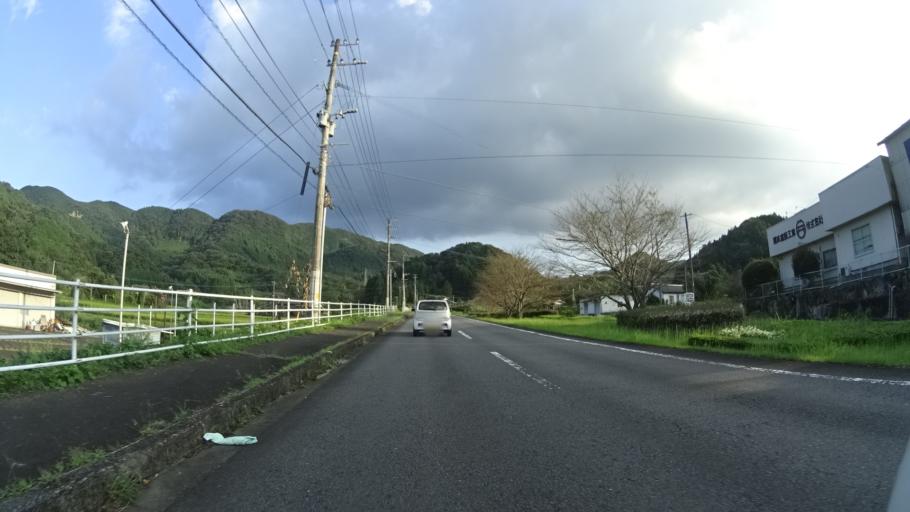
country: JP
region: Oita
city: Hiji
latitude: 33.3741
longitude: 131.3952
